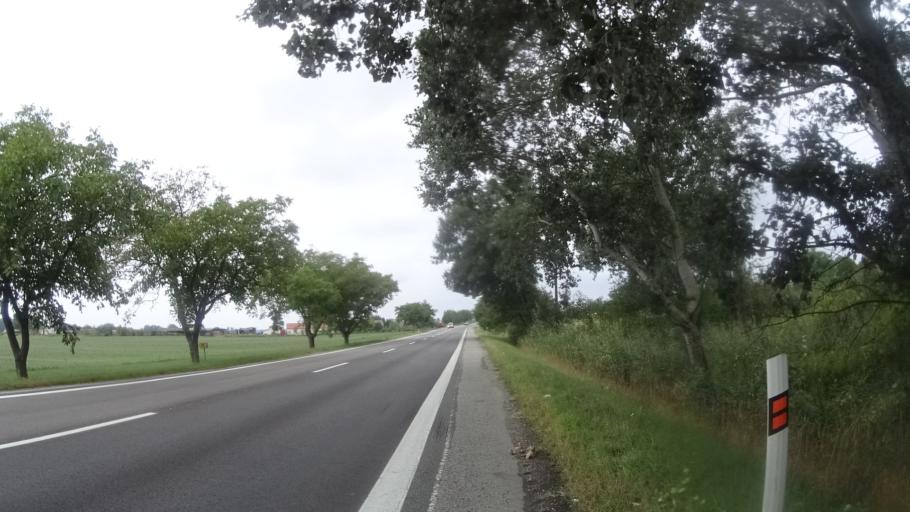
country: HU
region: Komarom-Esztergom
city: Acs
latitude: 47.7663
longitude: 18.0313
